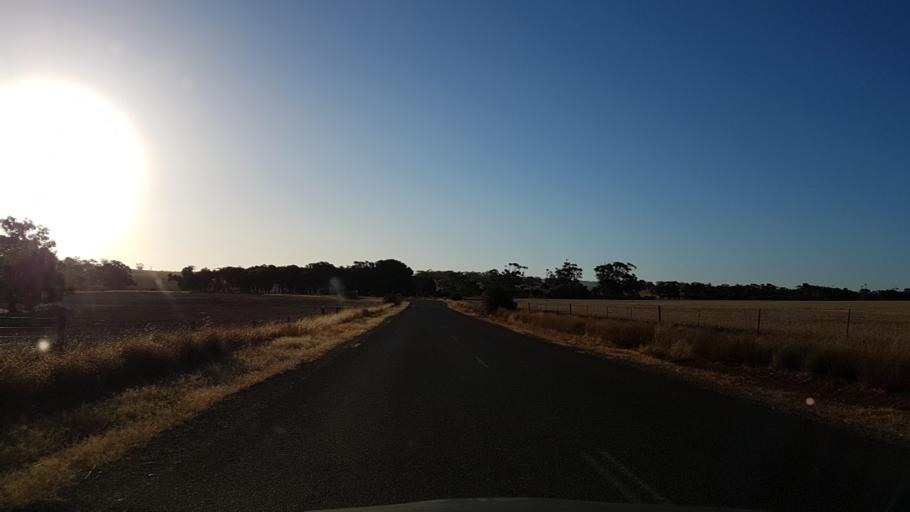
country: AU
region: South Australia
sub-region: Clare and Gilbert Valleys
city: Clare
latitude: -33.9986
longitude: 138.7441
